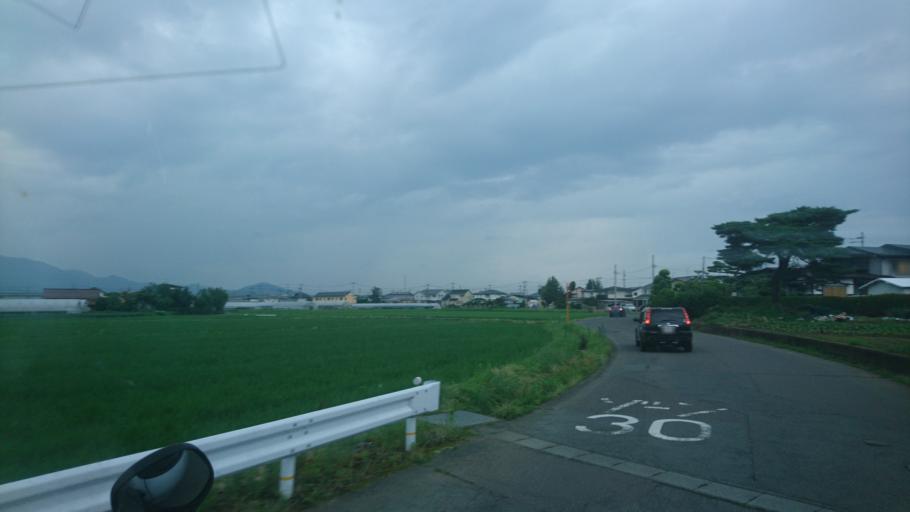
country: JP
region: Iwate
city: Morioka-shi
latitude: 39.6463
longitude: 141.1565
